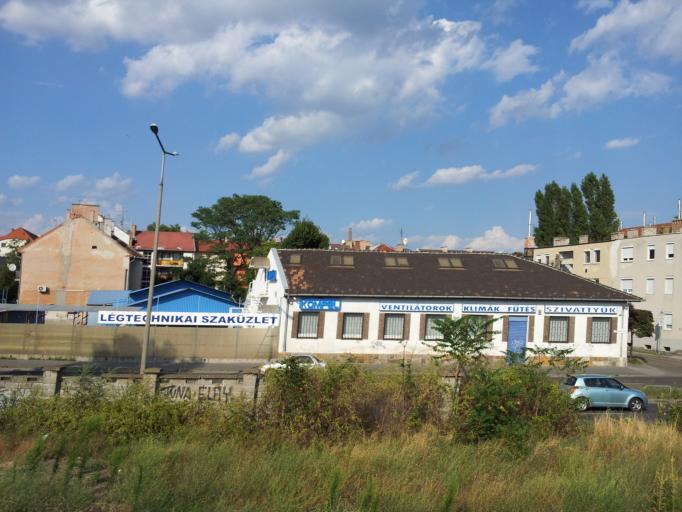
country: HU
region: Budapest
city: Budapest X. keruelet
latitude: 47.4762
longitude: 19.1325
